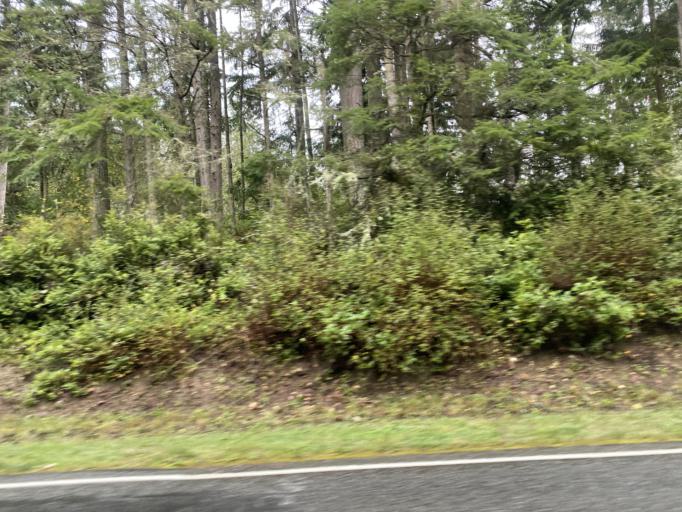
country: US
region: Washington
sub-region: Island County
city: Freeland
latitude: 48.0659
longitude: -122.4957
